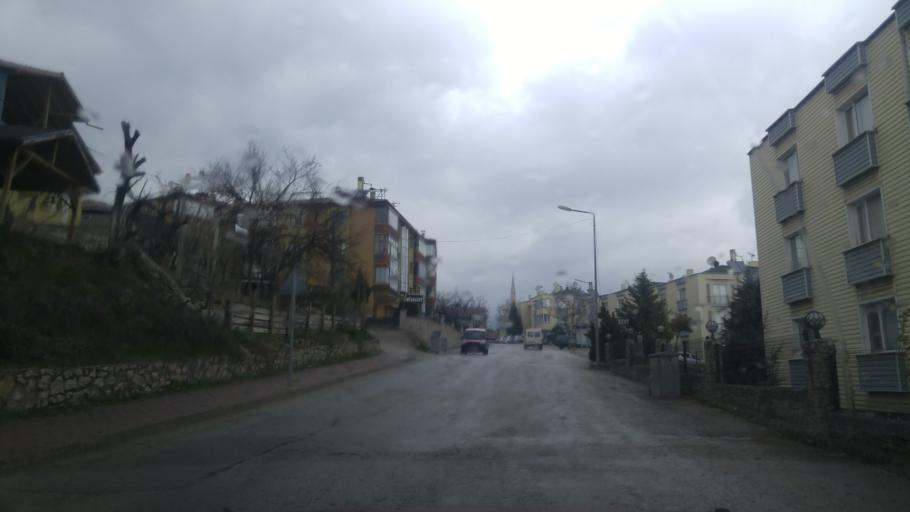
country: TR
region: Karabuk
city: Safranbolu
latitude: 41.2611
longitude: 32.6811
